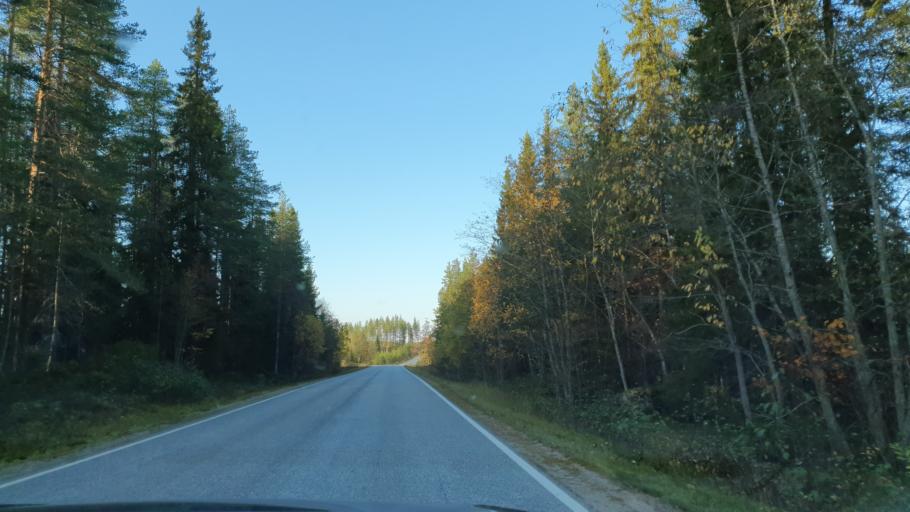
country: FI
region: Kainuu
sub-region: Kehys-Kainuu
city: Kuhmo
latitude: 64.3626
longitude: 29.4888
